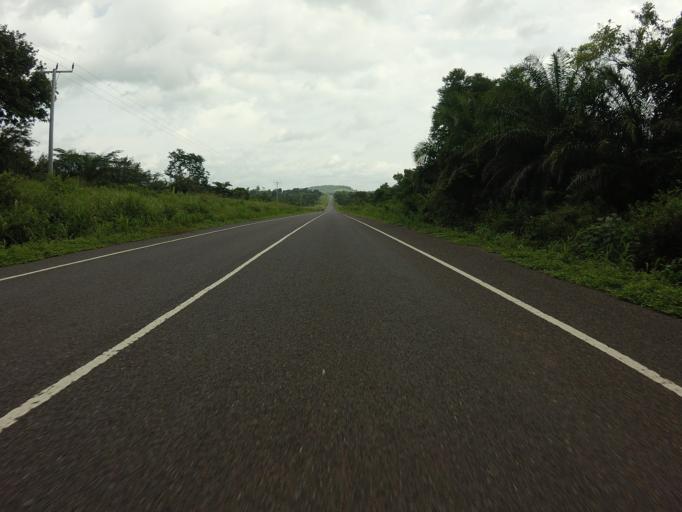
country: TG
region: Plateaux
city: Badou
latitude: 7.9776
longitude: 0.5600
